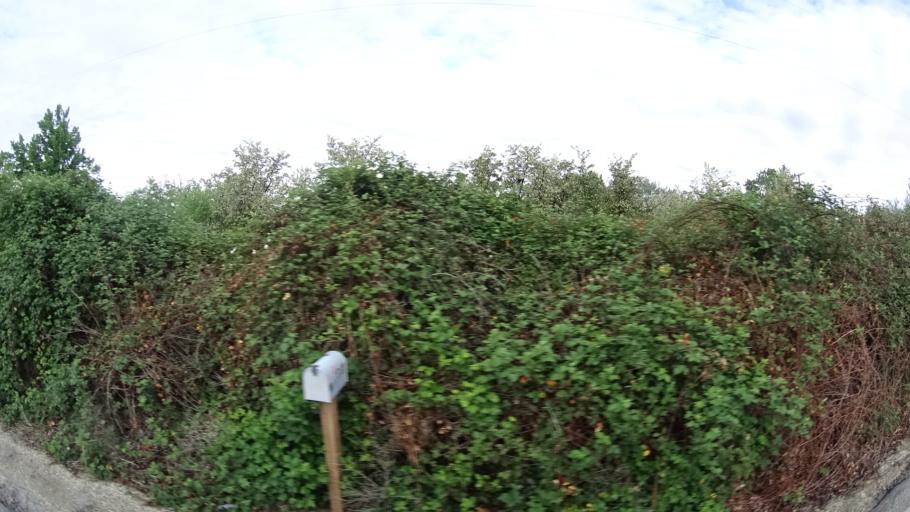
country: US
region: Idaho
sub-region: Ada County
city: Star
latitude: 43.7201
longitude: -116.5128
